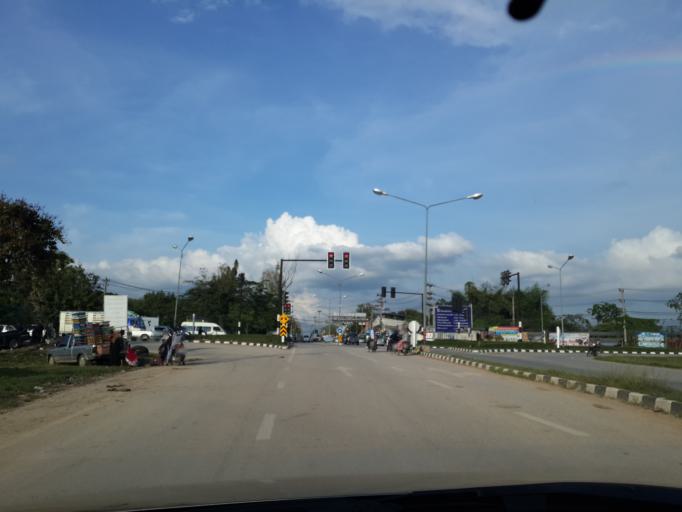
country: TH
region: Yala
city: Yala
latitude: 6.5134
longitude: 101.2724
